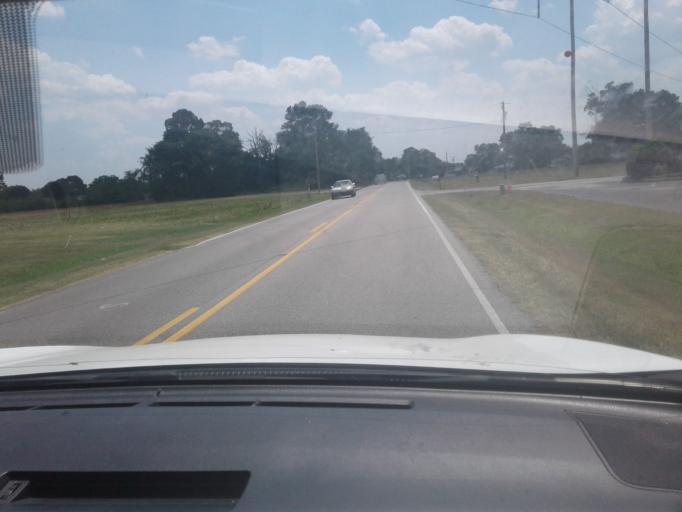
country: US
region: North Carolina
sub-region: Harnett County
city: Erwin
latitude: 35.3431
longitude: -78.6436
